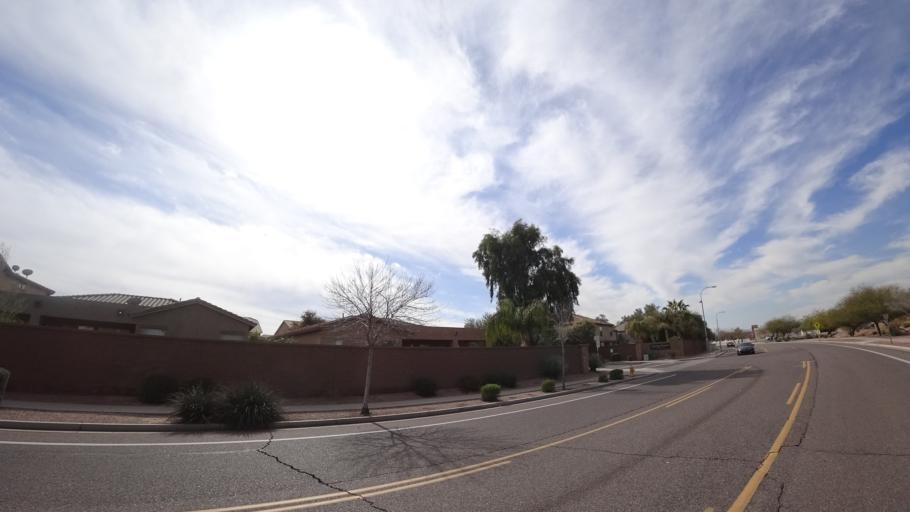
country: US
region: Arizona
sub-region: Maricopa County
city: Tolleson
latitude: 33.4728
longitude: -112.2595
